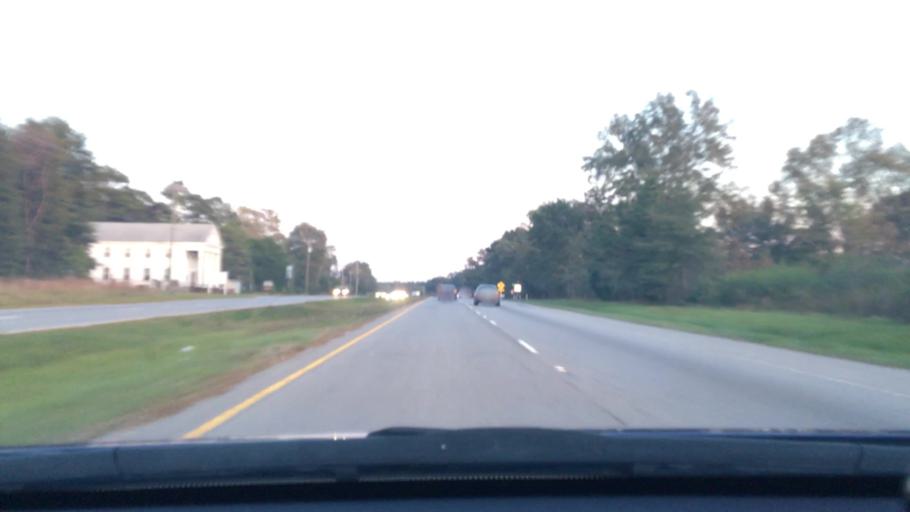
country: US
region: South Carolina
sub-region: Richland County
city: Gadsden
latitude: 33.9393
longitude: -80.7124
